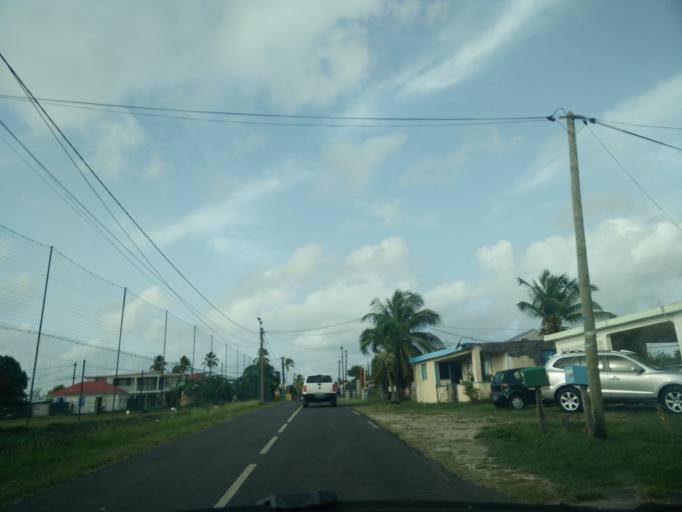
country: GP
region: Guadeloupe
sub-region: Guadeloupe
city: Le Moule
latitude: 16.2958
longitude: -61.3673
